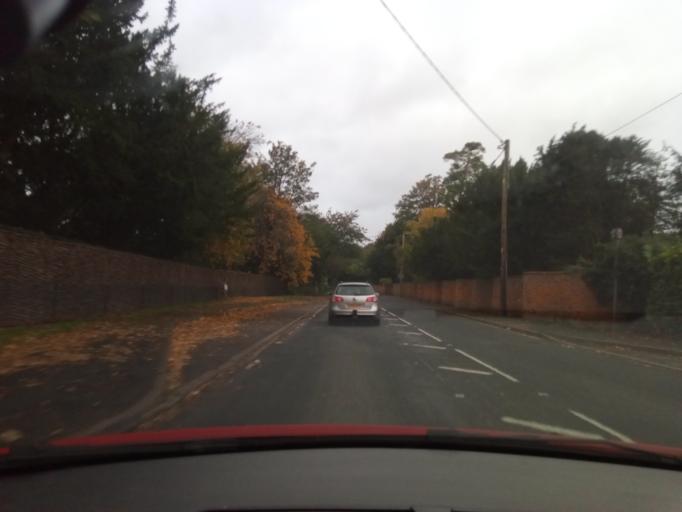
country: GB
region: England
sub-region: Essex
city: Great Yeldham
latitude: 52.0190
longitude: 0.5601
